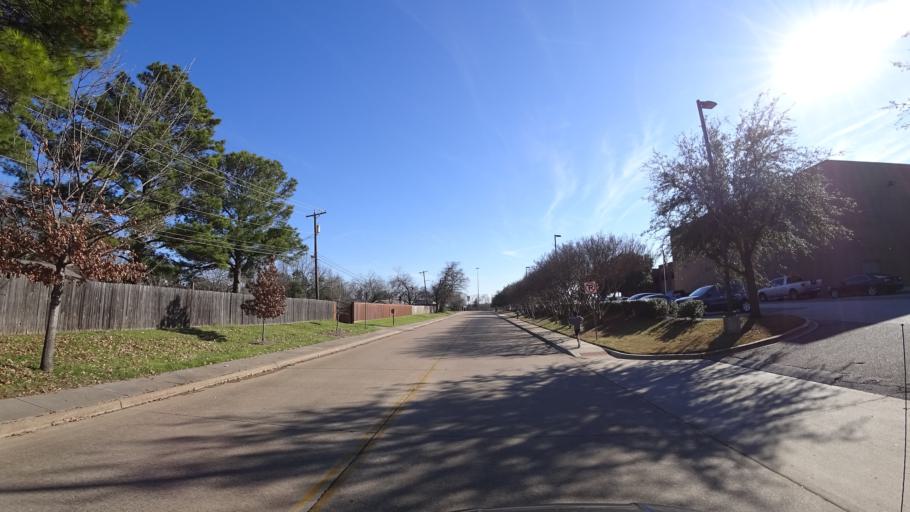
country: US
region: Texas
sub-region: Denton County
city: Highland Village
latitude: 33.0750
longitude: -97.0186
